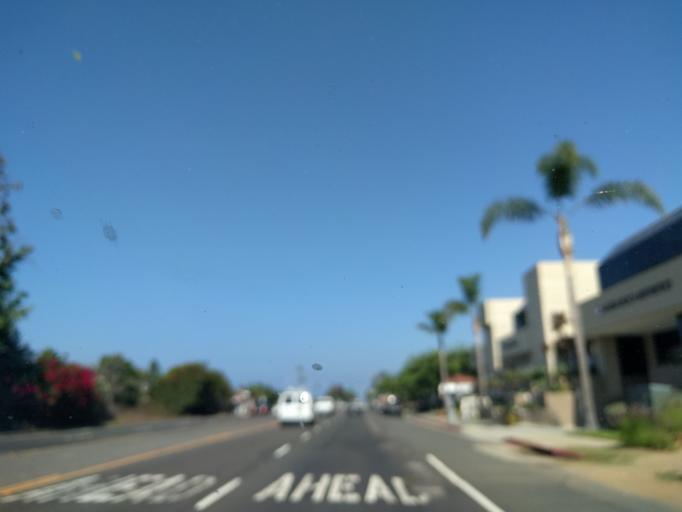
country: US
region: California
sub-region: Orange County
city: Laguna Niguel
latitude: 33.4918
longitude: -117.7334
